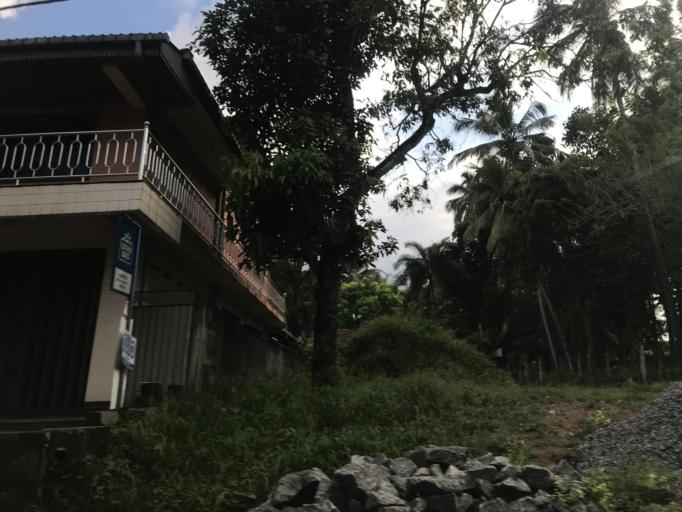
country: LK
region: Western
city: Gampaha
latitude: 7.0735
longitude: 79.9978
